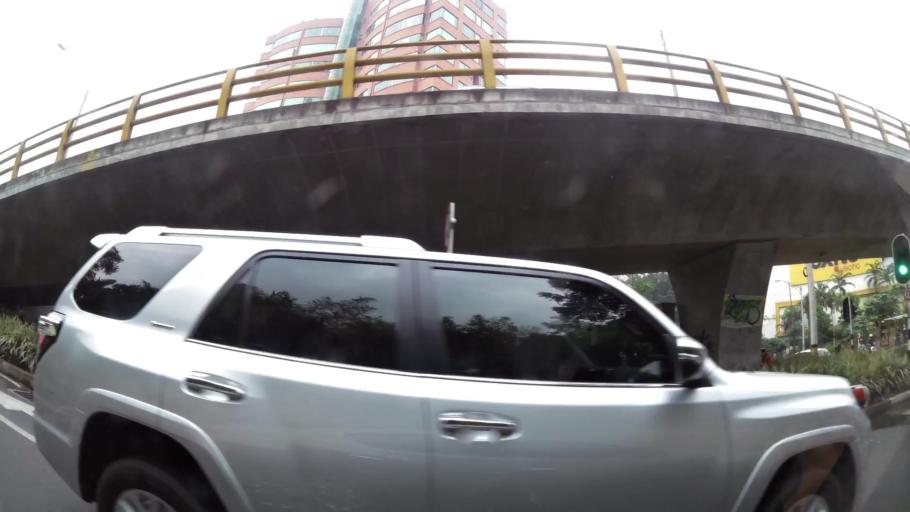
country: CO
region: Antioquia
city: Envigado
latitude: 6.1976
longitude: -75.5571
